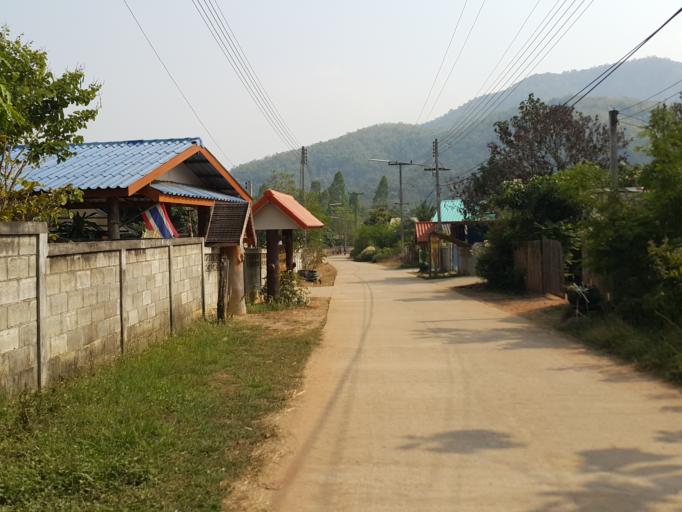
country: TH
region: Sukhothai
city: Thung Saliam
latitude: 17.3341
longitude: 99.4811
